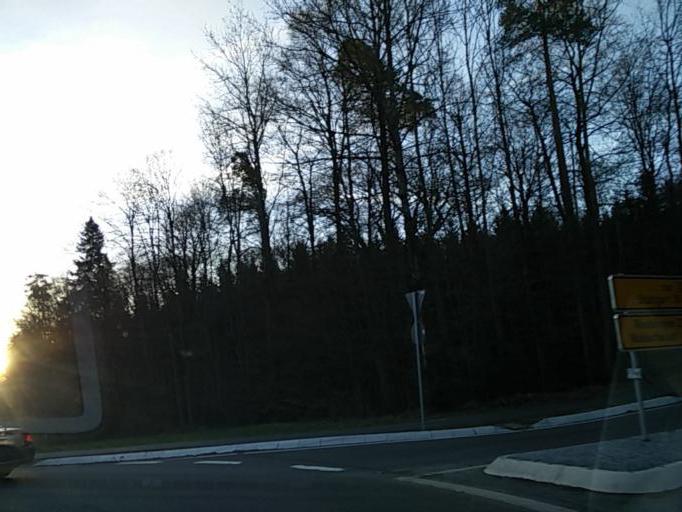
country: DE
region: Baden-Wuerttemberg
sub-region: Tuebingen Region
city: Dettenhausen
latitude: 48.5928
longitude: 9.0741
